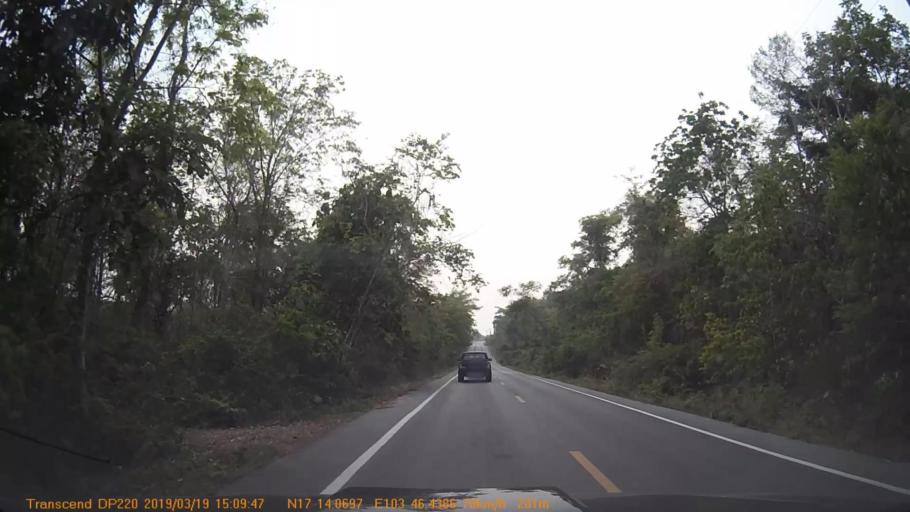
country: TH
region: Sakon Nakhon
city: Nikhom Nam Un
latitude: 17.2347
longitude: 103.7735
